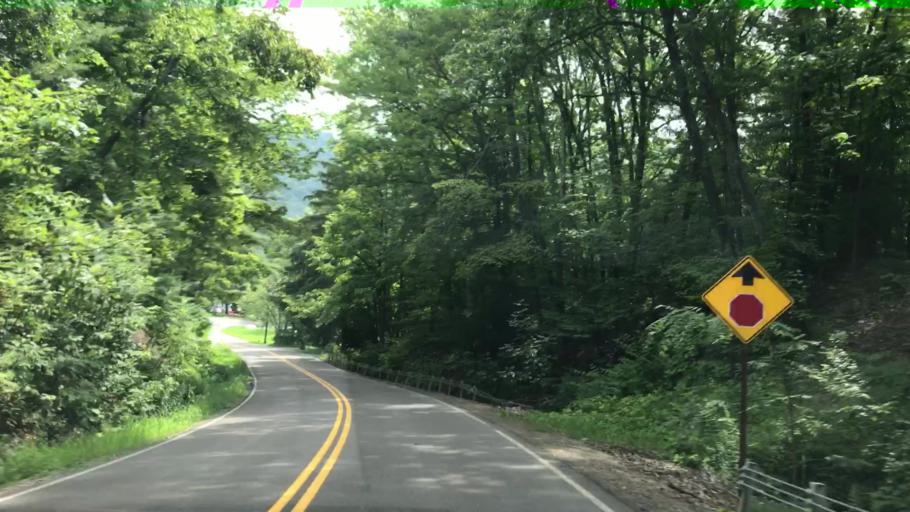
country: US
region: New York
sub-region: Steuben County
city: Sylvan Beach
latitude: 42.5286
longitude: -77.1547
